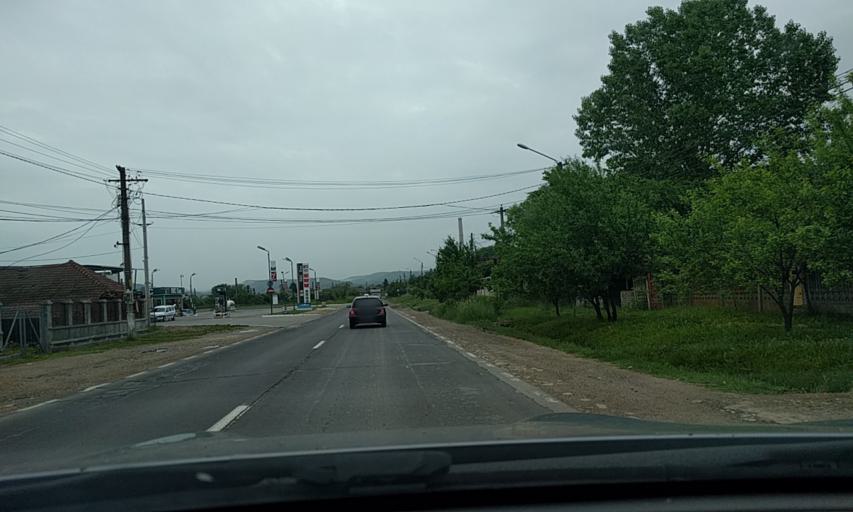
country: RO
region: Dambovita
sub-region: Comuna Doicesti
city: Doicesti
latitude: 44.9881
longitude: 25.4118
